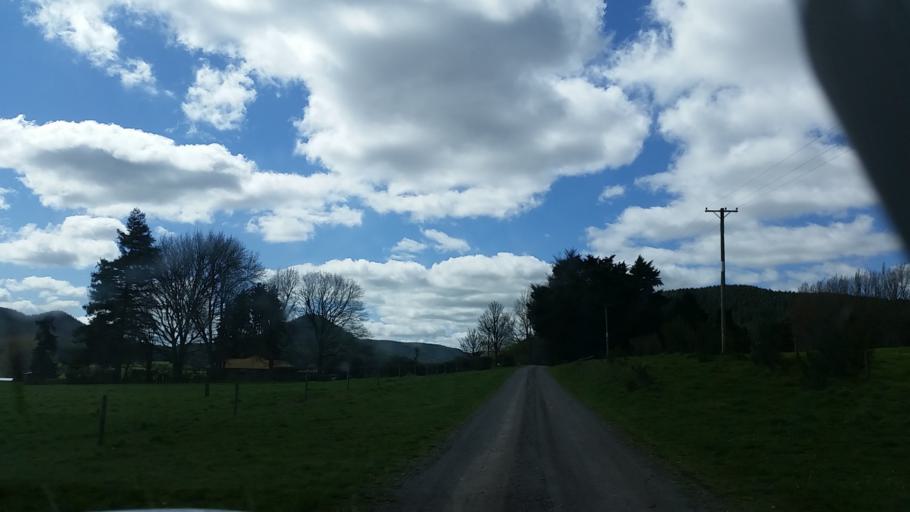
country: NZ
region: Bay of Plenty
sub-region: Rotorua District
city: Rotorua
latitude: -38.3931
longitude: 176.3921
